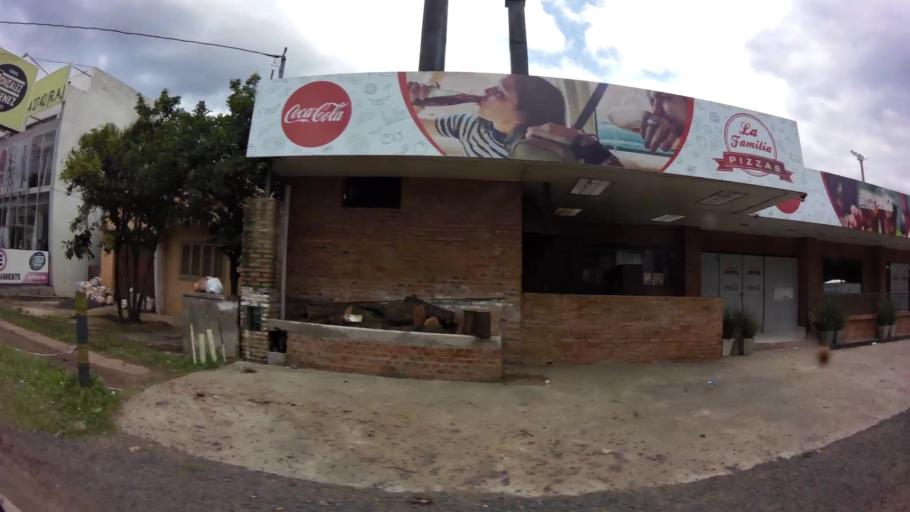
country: PY
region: Central
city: San Lorenzo
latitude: -25.2658
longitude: -57.5000
